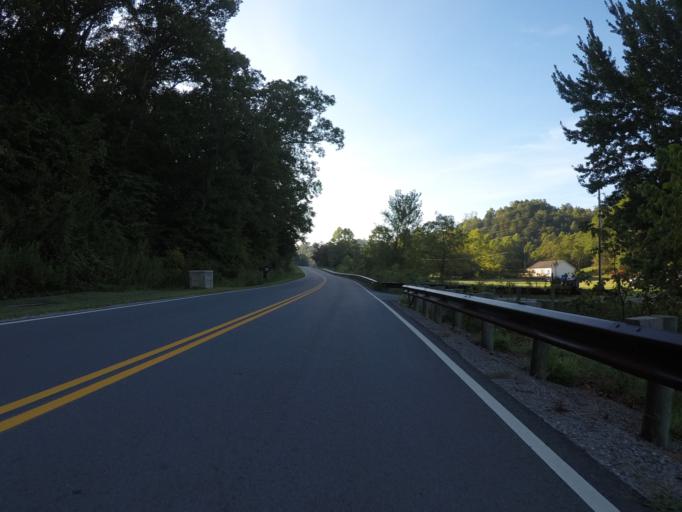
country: US
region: Ohio
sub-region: Lawrence County
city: Ironton
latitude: 38.6094
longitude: -82.5892
